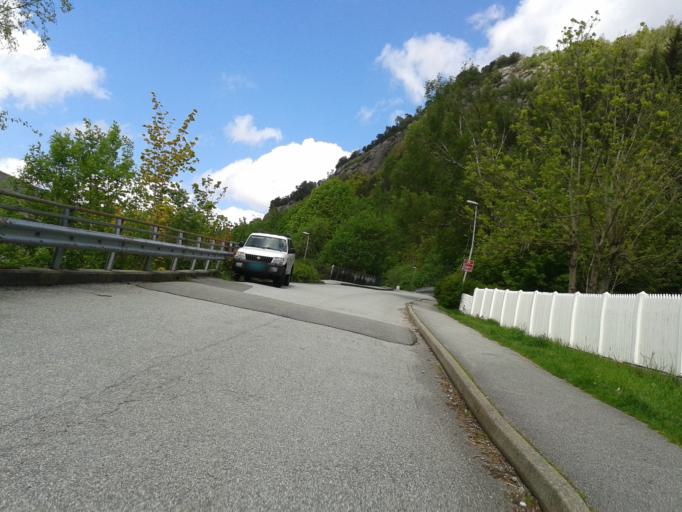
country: NO
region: Hordaland
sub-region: Bergen
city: Bergen
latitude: 60.4138
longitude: 5.3230
